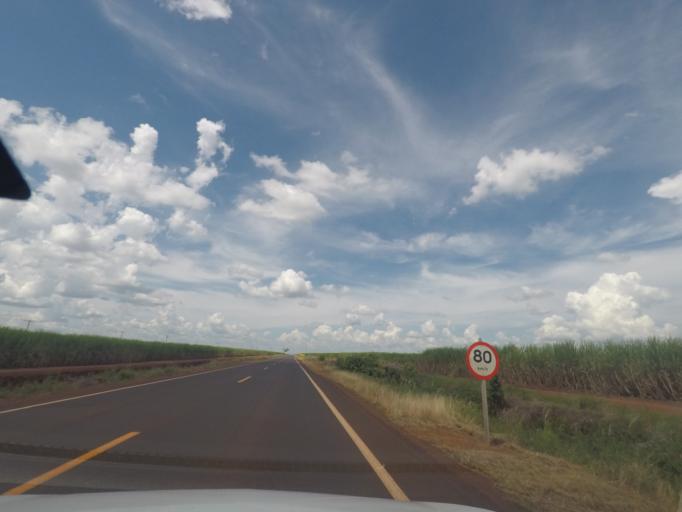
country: BR
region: Minas Gerais
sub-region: Conceicao Das Alagoas
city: Conceicao das Alagoas
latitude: -19.8668
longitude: -48.6128
